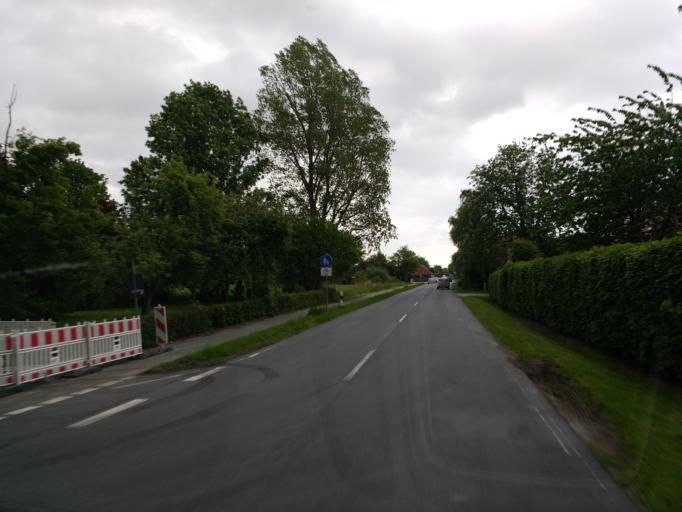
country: DE
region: Lower Saxony
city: Schillig
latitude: 53.6383
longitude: 8.0075
